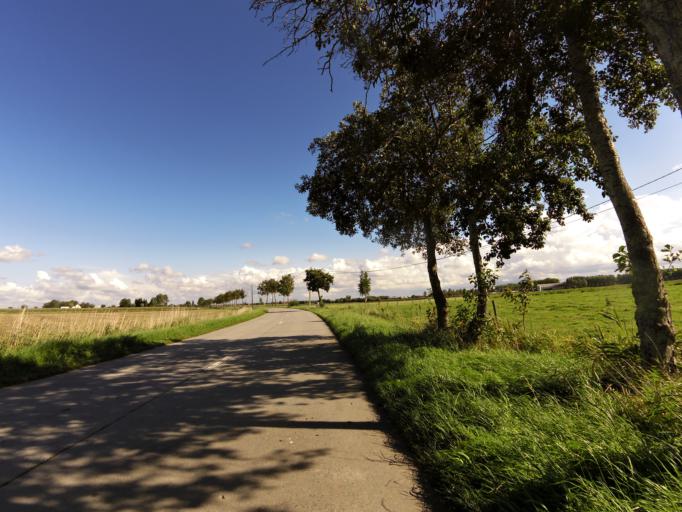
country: BE
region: Flanders
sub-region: Provincie West-Vlaanderen
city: Gistel
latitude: 51.1415
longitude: 2.8969
